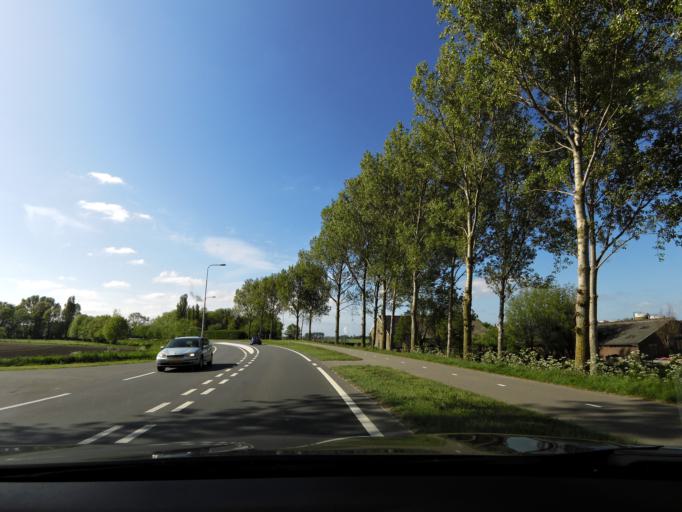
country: NL
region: South Holland
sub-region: Gemeente Hellevoetsluis
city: Nieuwenhoorn
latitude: 51.8663
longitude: 4.1139
